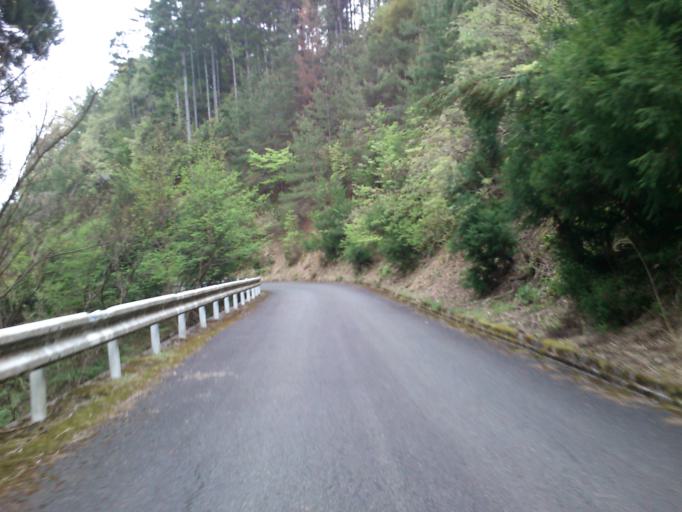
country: JP
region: Kyoto
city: Maizuru
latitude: 35.3847
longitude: 135.4411
